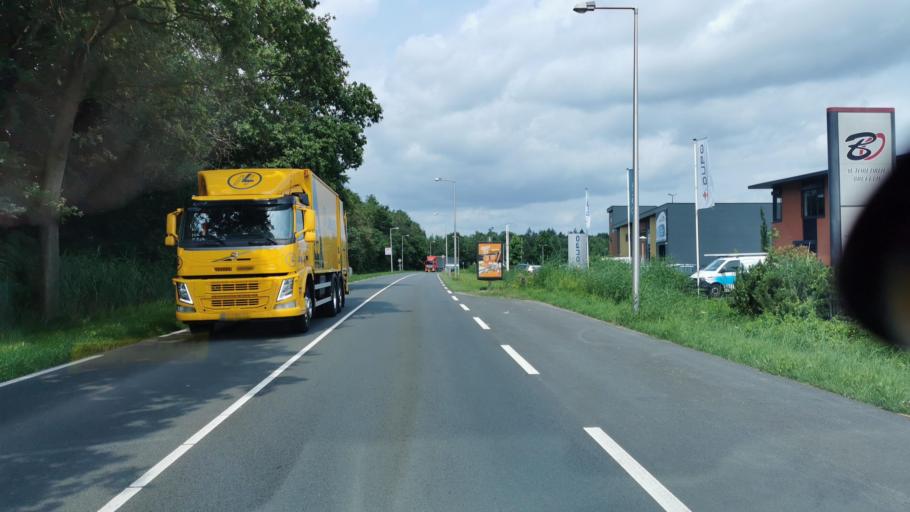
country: NL
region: Overijssel
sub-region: Gemeente Enschede
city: Enschede
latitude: 52.2234
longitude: 6.9404
